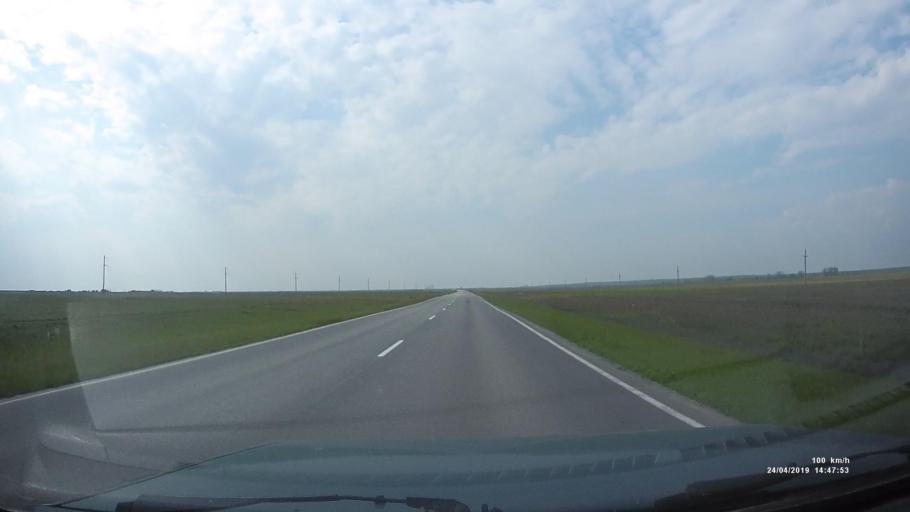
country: RU
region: Rostov
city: Remontnoye
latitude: 46.4957
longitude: 43.7655
